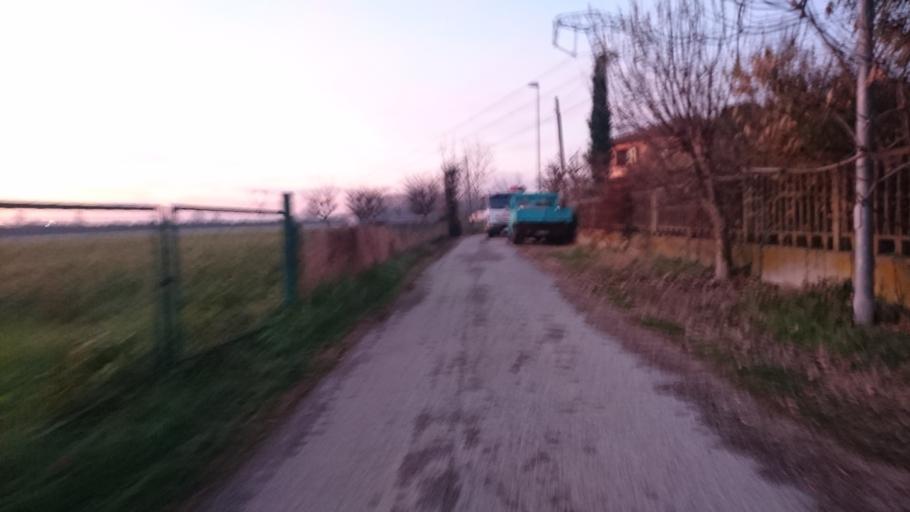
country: IT
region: Veneto
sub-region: Provincia di Padova
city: Albignasego
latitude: 45.3538
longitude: 11.9002
